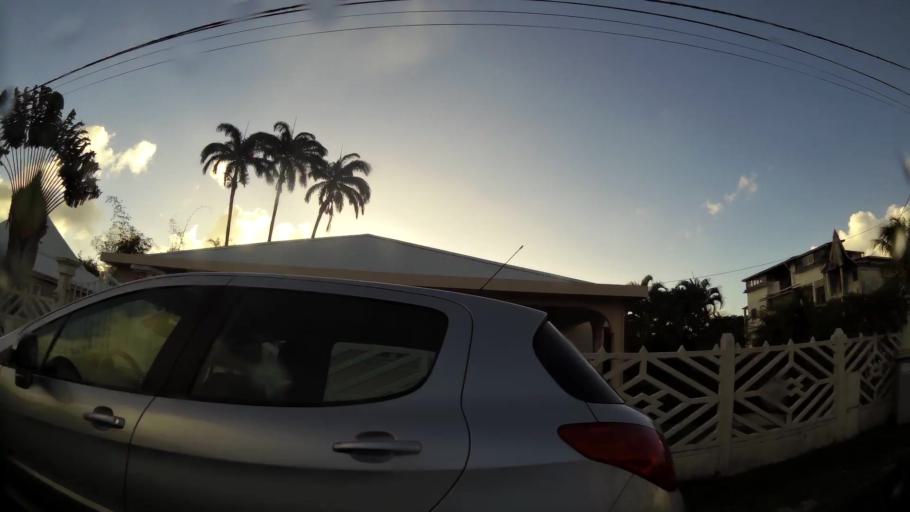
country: MQ
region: Martinique
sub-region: Martinique
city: Fort-de-France
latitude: 14.6236
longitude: -61.0721
